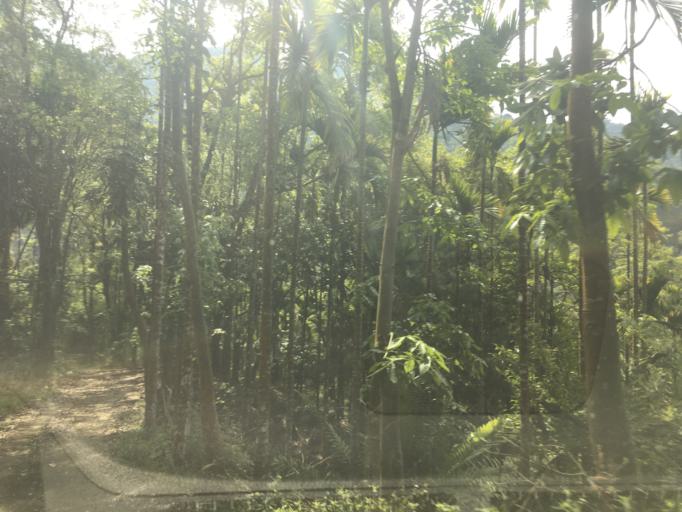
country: TW
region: Taiwan
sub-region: Taichung City
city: Taichung
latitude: 24.1305
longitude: 120.8242
